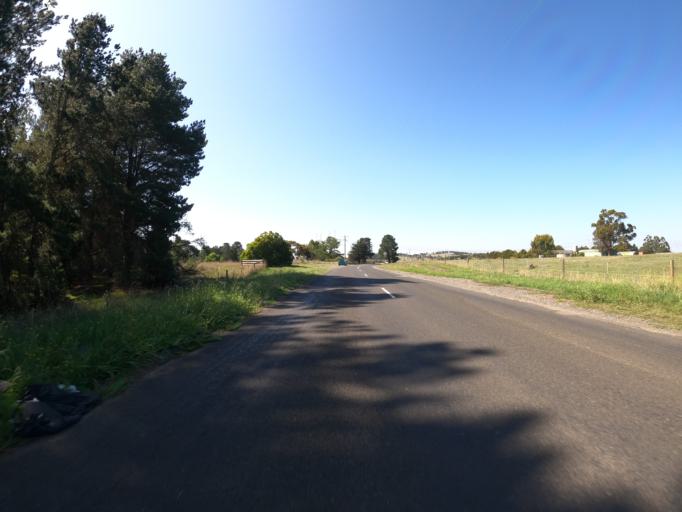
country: AU
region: Victoria
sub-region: Hume
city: Greenvale
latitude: -37.5488
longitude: 144.8687
